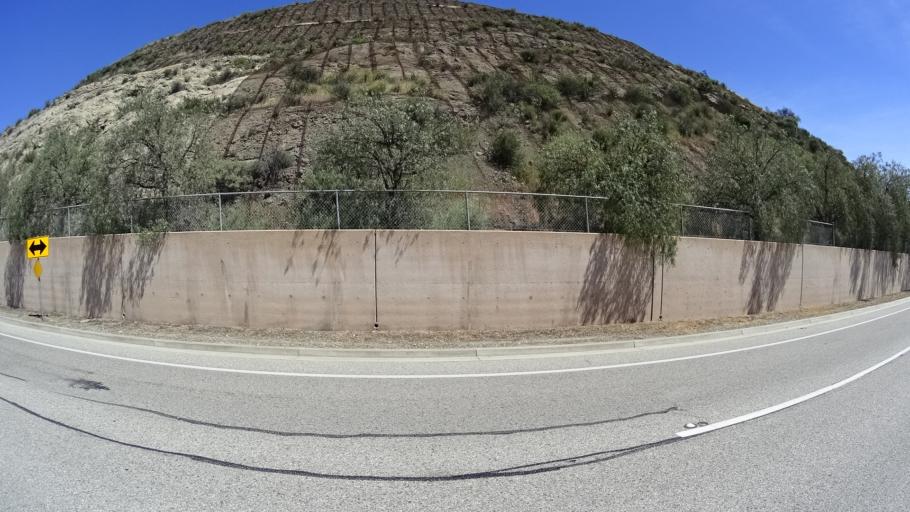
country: US
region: California
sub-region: Ventura County
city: Thousand Oaks
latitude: 34.1426
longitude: -118.8634
